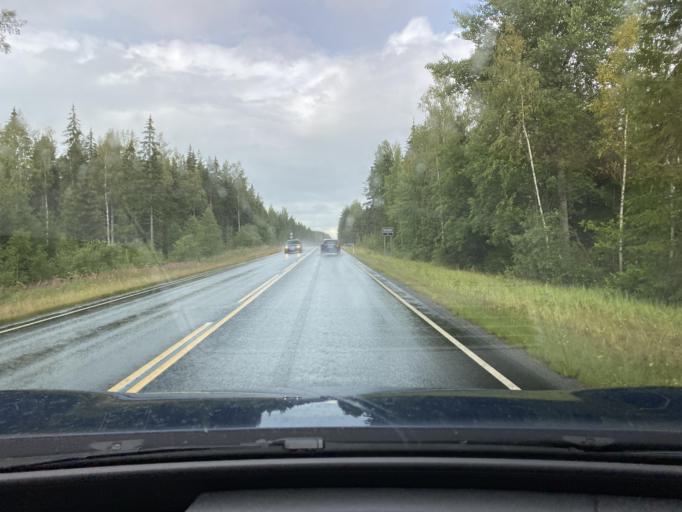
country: FI
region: Pirkanmaa
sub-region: Tampere
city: Haemeenkyroe
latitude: 61.5885
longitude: 23.1102
